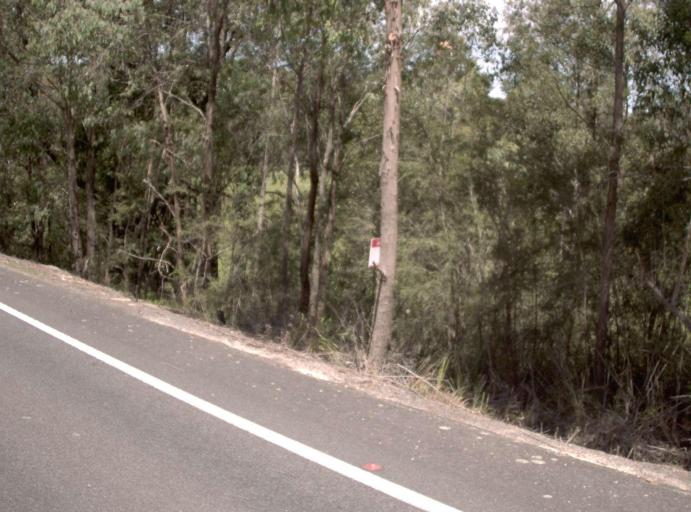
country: AU
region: New South Wales
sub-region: Bombala
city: Bombala
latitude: -37.5656
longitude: 149.0790
